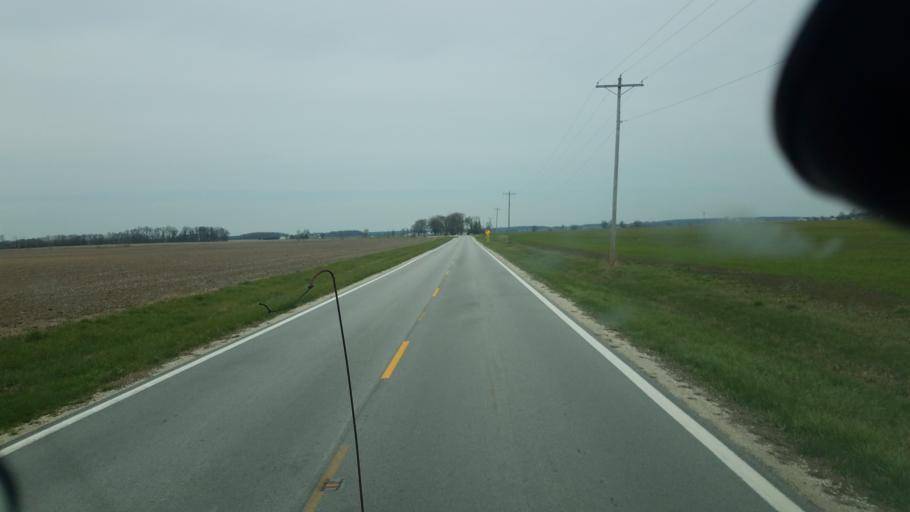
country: US
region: Ohio
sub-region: Wyandot County
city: Carey
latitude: 40.9857
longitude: -83.4766
